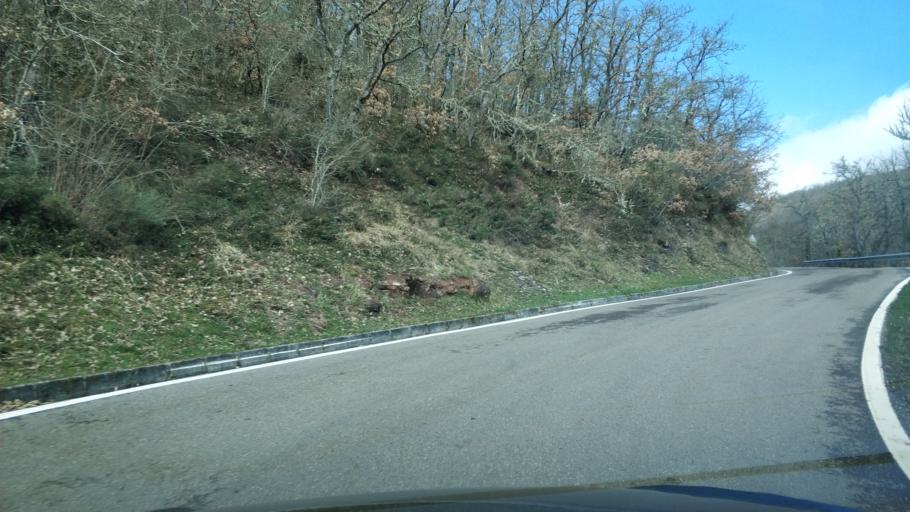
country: ES
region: Castille and Leon
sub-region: Provincia de Palencia
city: Berzosilla
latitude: 42.8979
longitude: -4.0414
